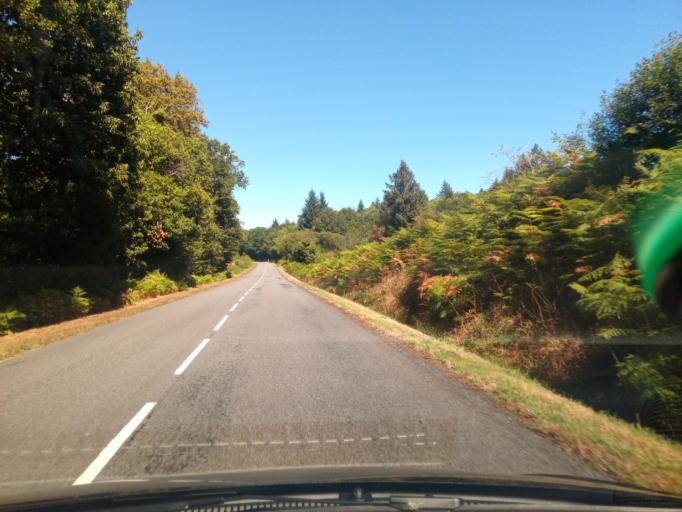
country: FR
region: Limousin
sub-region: Departement de la Haute-Vienne
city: Nantiat
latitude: 46.0696
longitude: 1.2032
